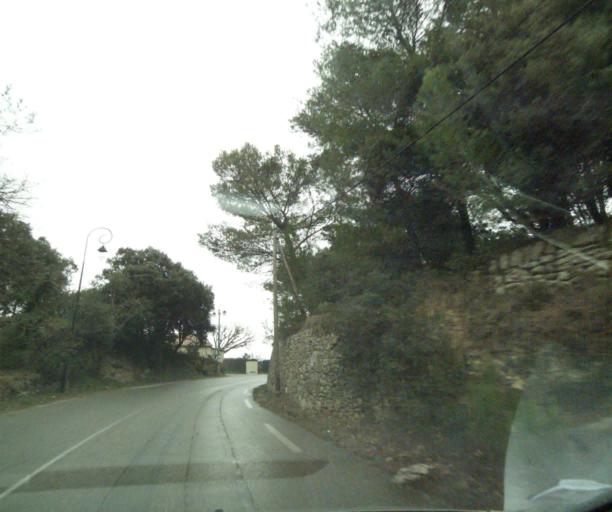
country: FR
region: Provence-Alpes-Cote d'Azur
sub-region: Departement des Bouches-du-Rhone
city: Rognes
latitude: 43.6639
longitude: 5.3396
